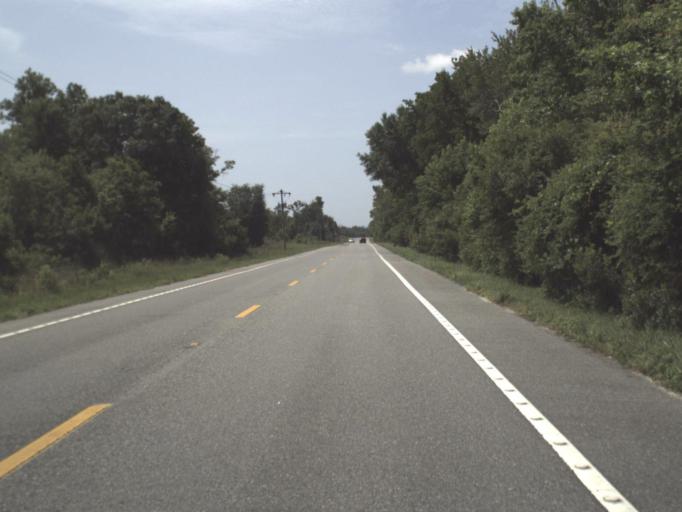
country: US
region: Florida
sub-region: Taylor County
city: Steinhatchee
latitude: 29.7231
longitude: -83.3605
